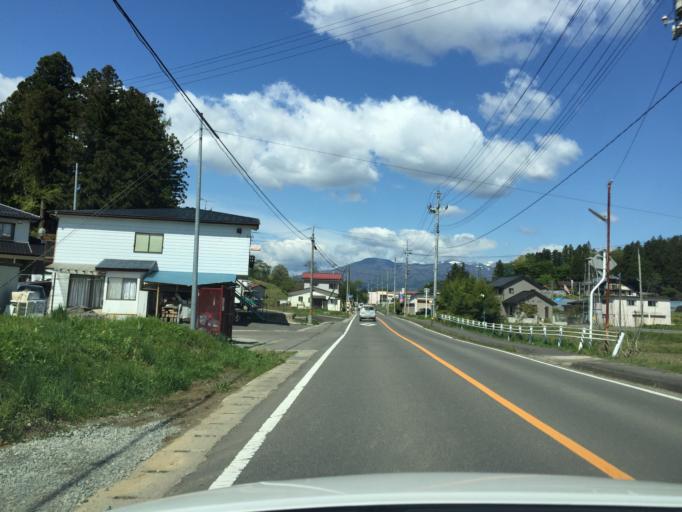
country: JP
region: Fukushima
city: Nihommatsu
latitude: 37.5752
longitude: 140.4667
